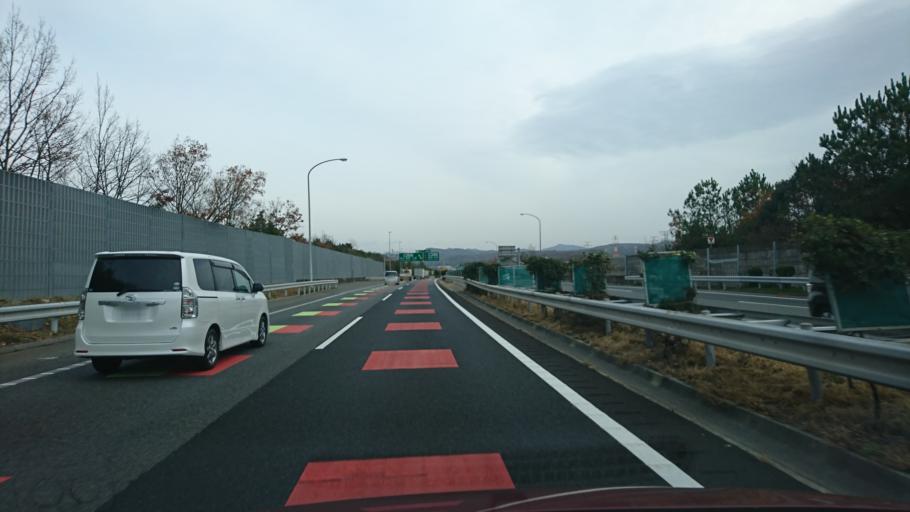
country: JP
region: Hyogo
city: Sandacho
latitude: 34.8466
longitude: 135.2077
